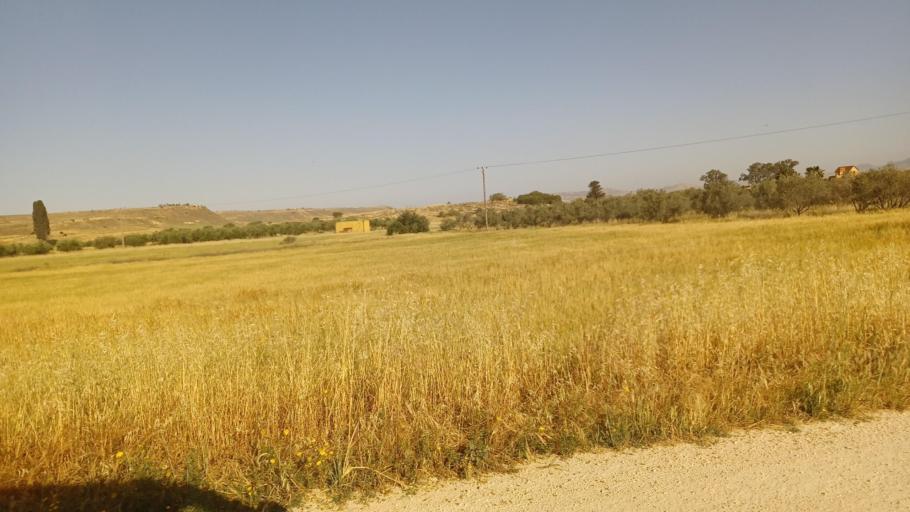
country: CY
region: Lefkosia
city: Mammari
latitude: 35.1646
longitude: 33.2494
